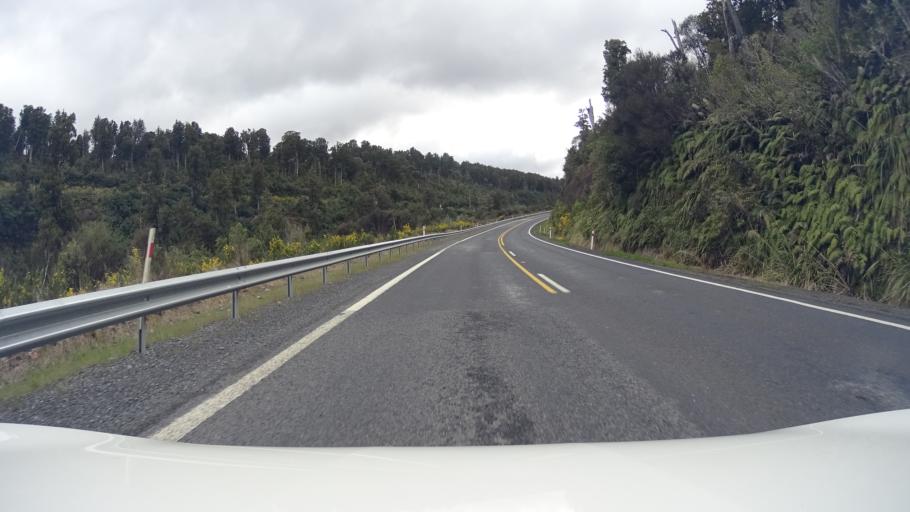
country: NZ
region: Manawatu-Wanganui
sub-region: Ruapehu District
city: Waiouru
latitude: -39.2655
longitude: 175.3932
